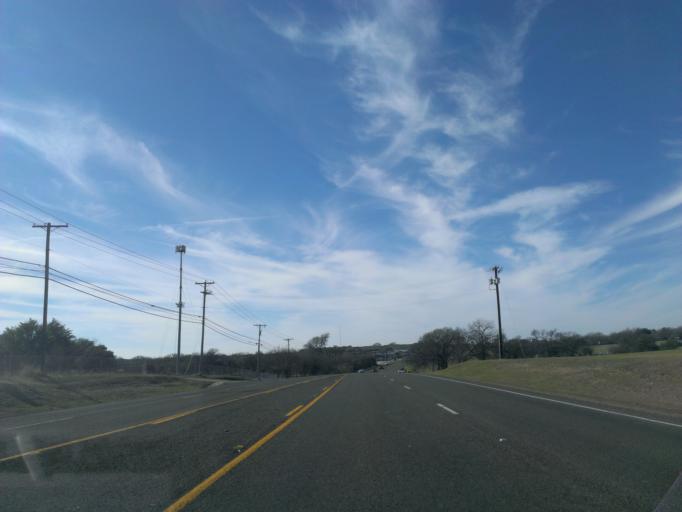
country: US
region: Texas
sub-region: Bell County
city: Harker Heights
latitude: 31.1160
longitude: -97.6860
